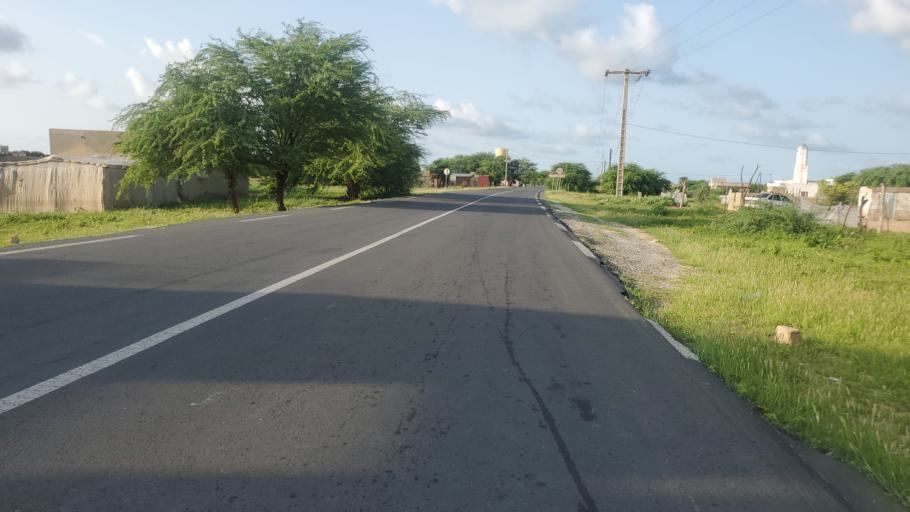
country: SN
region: Saint-Louis
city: Saint-Louis
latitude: 16.1335
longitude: -16.4119
